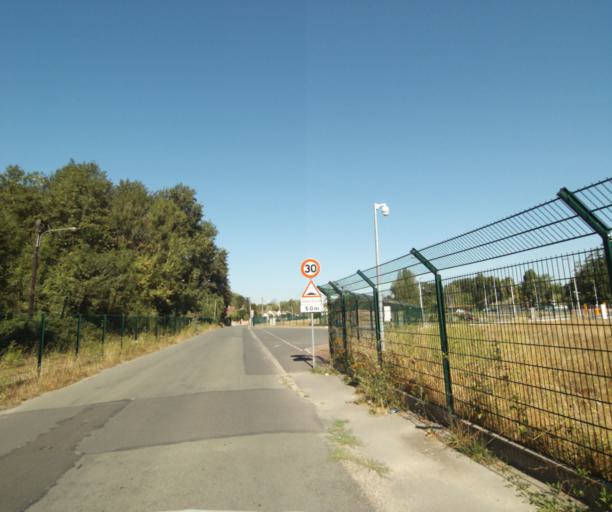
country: FR
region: Ile-de-France
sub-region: Departement de l'Essonne
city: Vert-le-Petit
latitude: 48.5335
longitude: 2.3592
